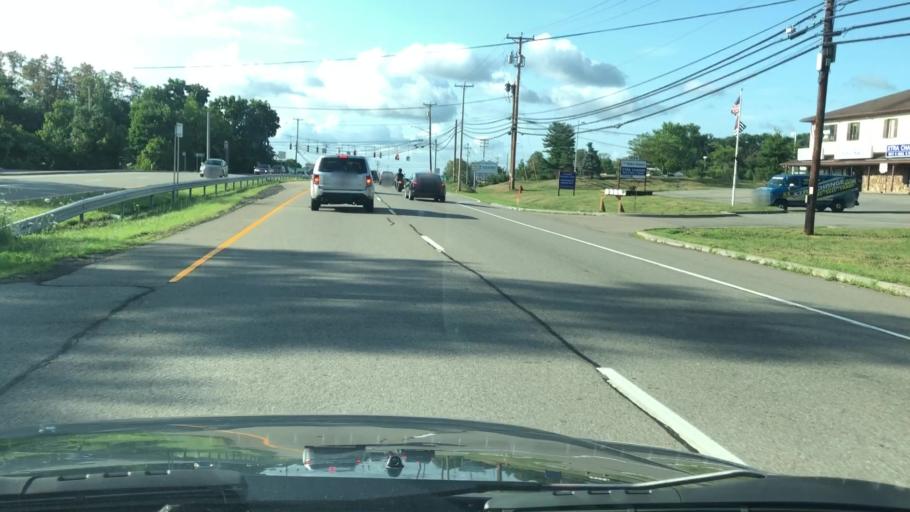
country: US
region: New York
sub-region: Dutchess County
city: Wappingers Falls
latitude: 41.5719
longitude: -73.9090
